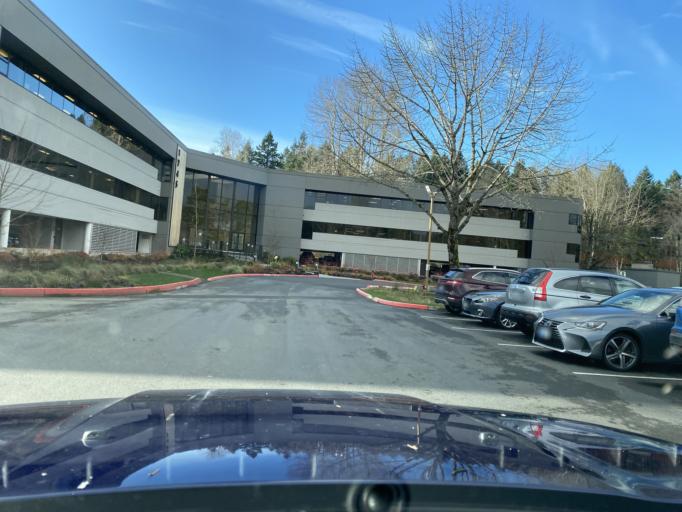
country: US
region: Washington
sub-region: King County
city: Bellevue
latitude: 47.5947
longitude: -122.1920
